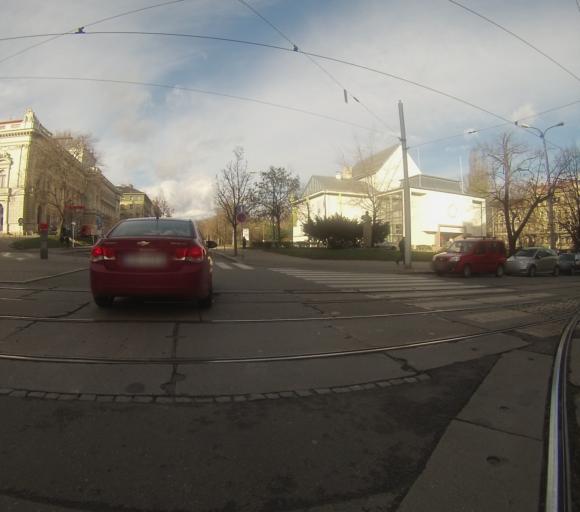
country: CZ
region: South Moravian
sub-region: Mesto Brno
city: Brno
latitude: 49.1958
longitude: 16.6146
